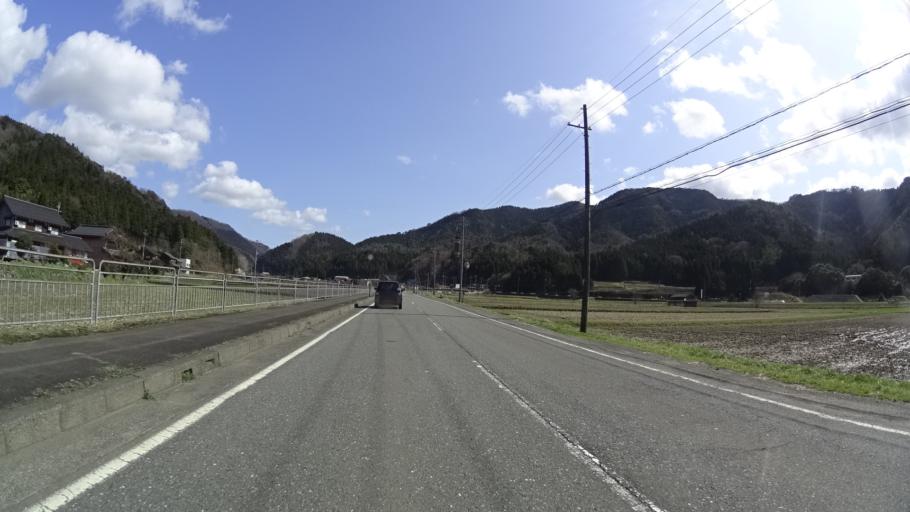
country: JP
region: Fukui
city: Obama
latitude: 35.4528
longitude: 135.8826
